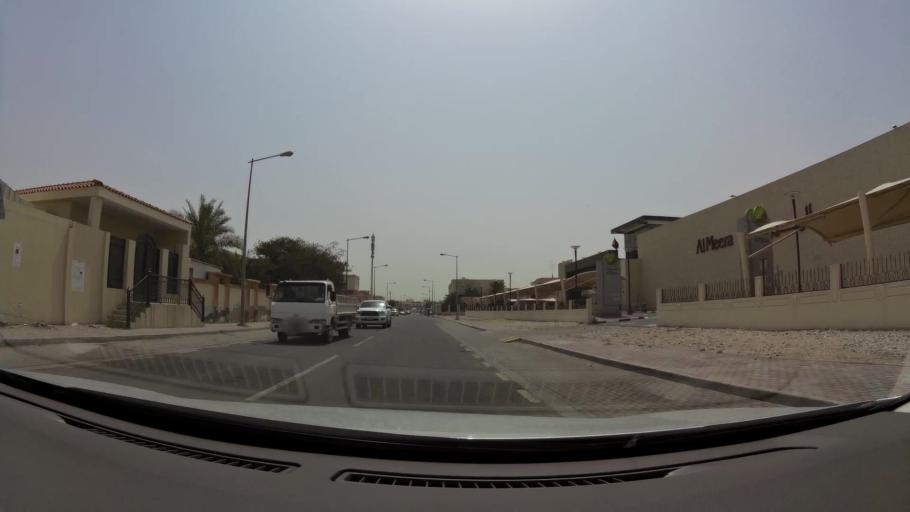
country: QA
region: Baladiyat ar Rayyan
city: Ar Rayyan
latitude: 25.2460
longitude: 51.4298
